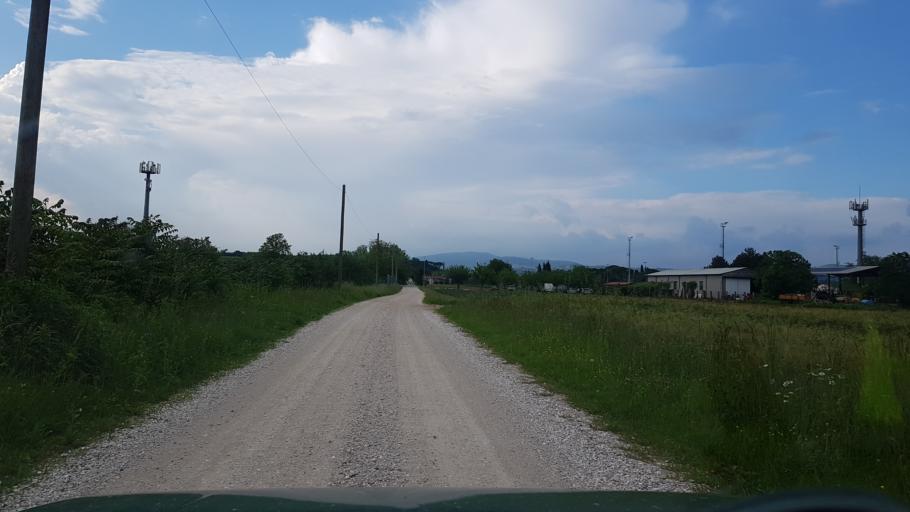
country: IT
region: Friuli Venezia Giulia
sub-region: Provincia di Gorizia
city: Mossa
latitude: 45.9280
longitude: 13.5427
